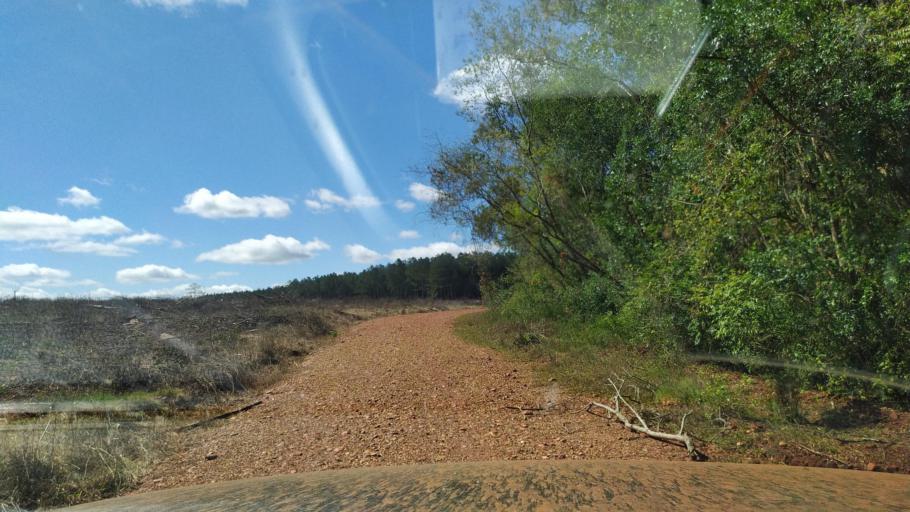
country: AR
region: Corrientes
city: Gobernador Ingeniero Valentin Virasoro
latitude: -28.2904
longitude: -56.0468
